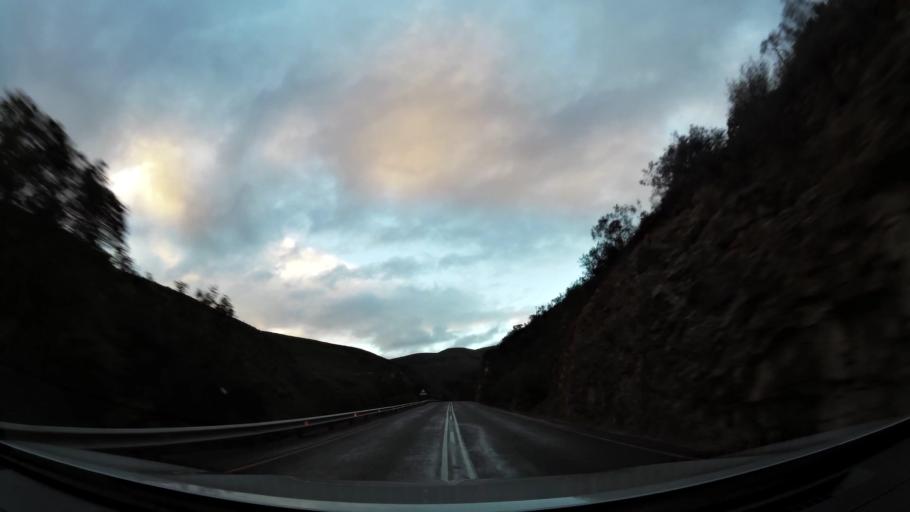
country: ZA
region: Western Cape
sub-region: Overberg District Municipality
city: Swellendam
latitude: -33.9936
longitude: 20.7051
